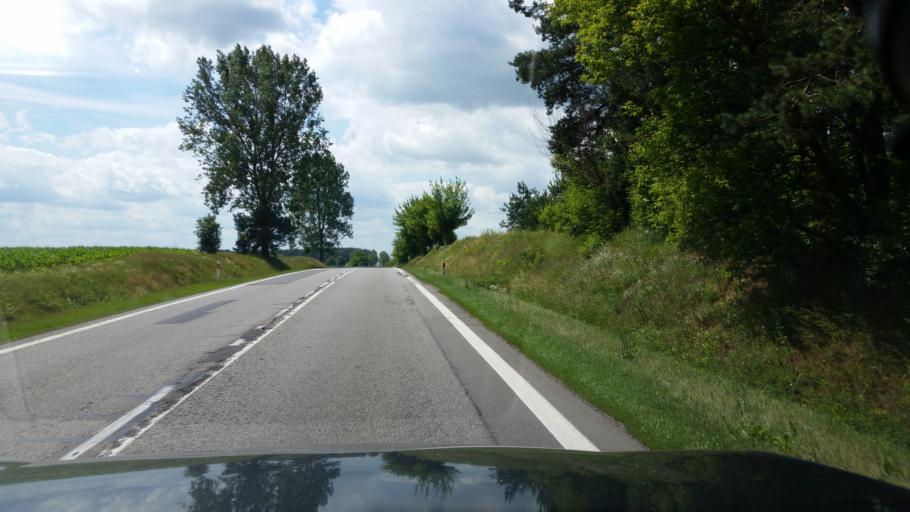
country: PL
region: Podlasie
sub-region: Powiat lomzynski
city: Piatnica
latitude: 53.2818
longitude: 22.1384
